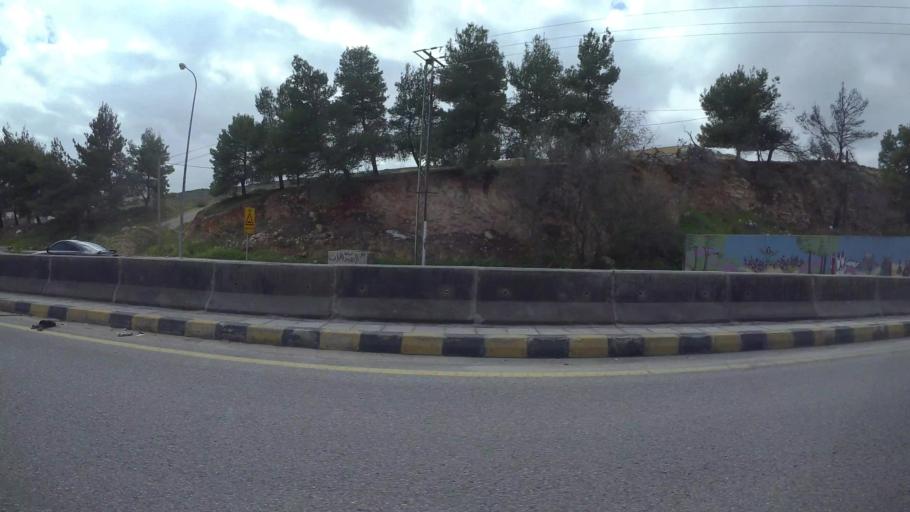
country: JO
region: Amman
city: Al Jubayhah
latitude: 32.0303
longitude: 35.7958
